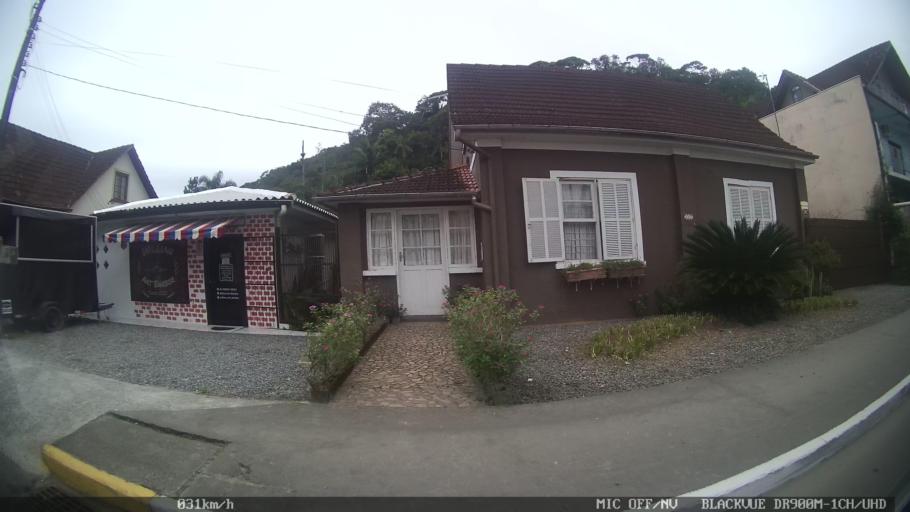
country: BR
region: Santa Catarina
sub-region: Joinville
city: Joinville
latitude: -26.2108
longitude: -48.9076
